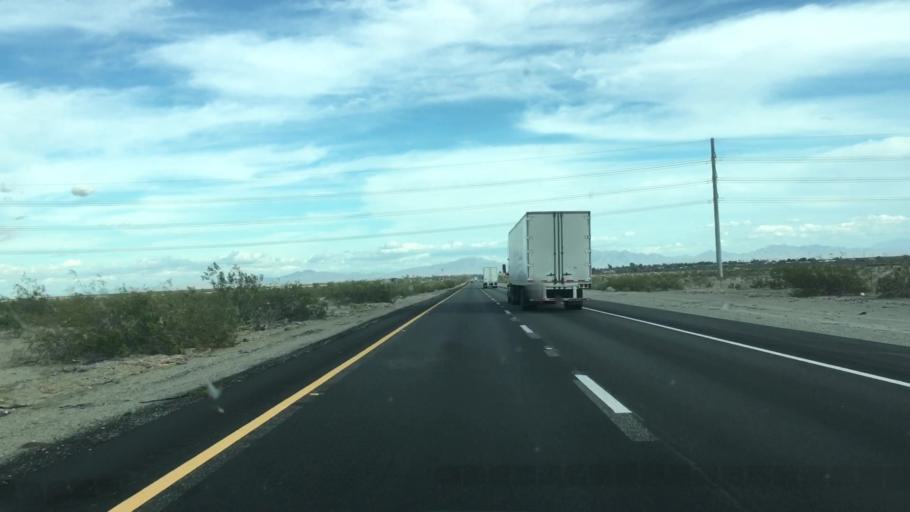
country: US
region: California
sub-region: Riverside County
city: Mesa Verde
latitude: 33.6088
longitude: -114.7551
